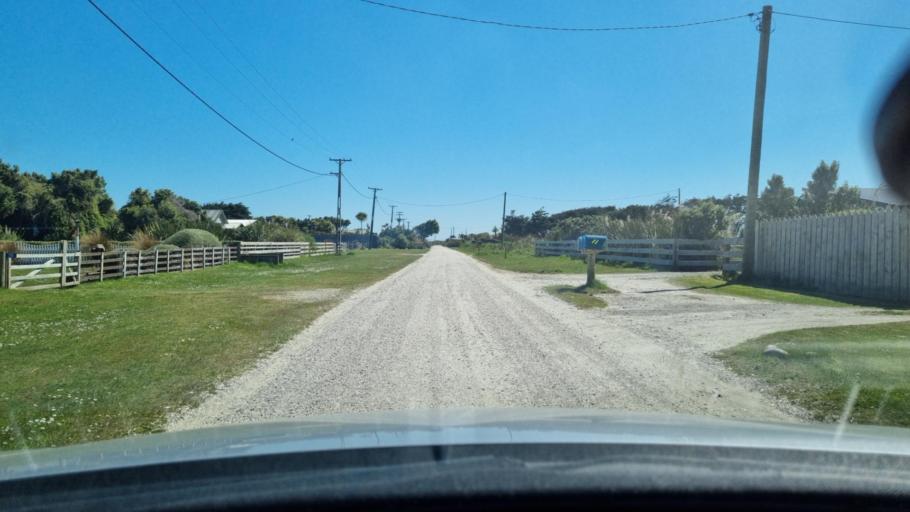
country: NZ
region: Southland
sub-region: Invercargill City
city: Invercargill
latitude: -46.4319
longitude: 168.2341
